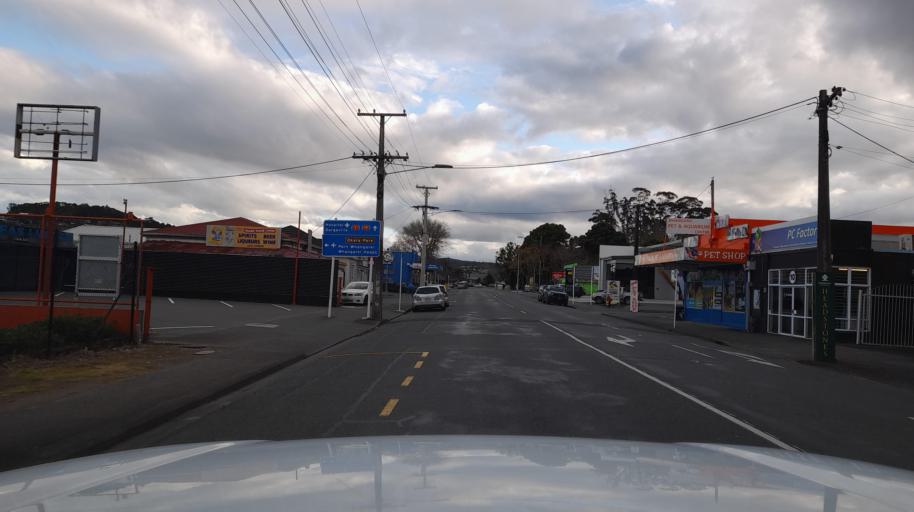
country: NZ
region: Northland
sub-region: Whangarei
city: Whangarei
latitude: -35.7278
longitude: 174.3163
